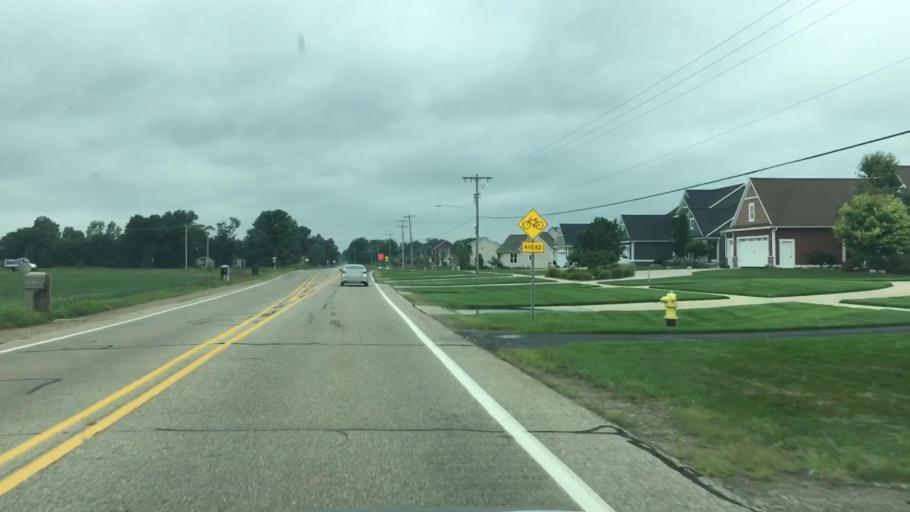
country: US
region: Michigan
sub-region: Ottawa County
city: Hudsonville
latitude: 42.8708
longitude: -85.8341
